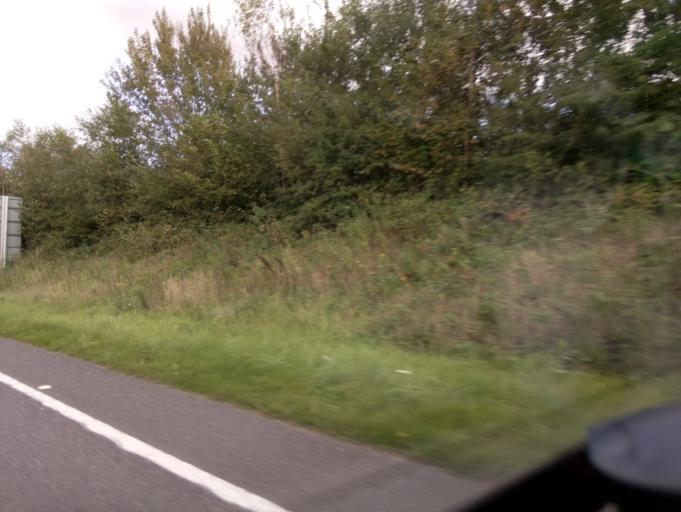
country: GB
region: Wales
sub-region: Rhondda Cynon Taf
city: Llantwit Fardre
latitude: 51.5567
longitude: -3.3177
